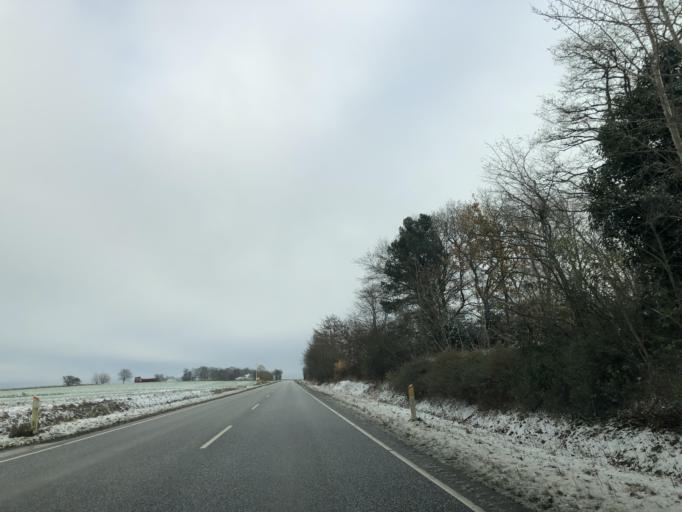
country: DK
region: Central Jutland
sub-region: Horsens Kommune
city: Braedstrup
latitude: 55.8929
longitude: 9.6555
